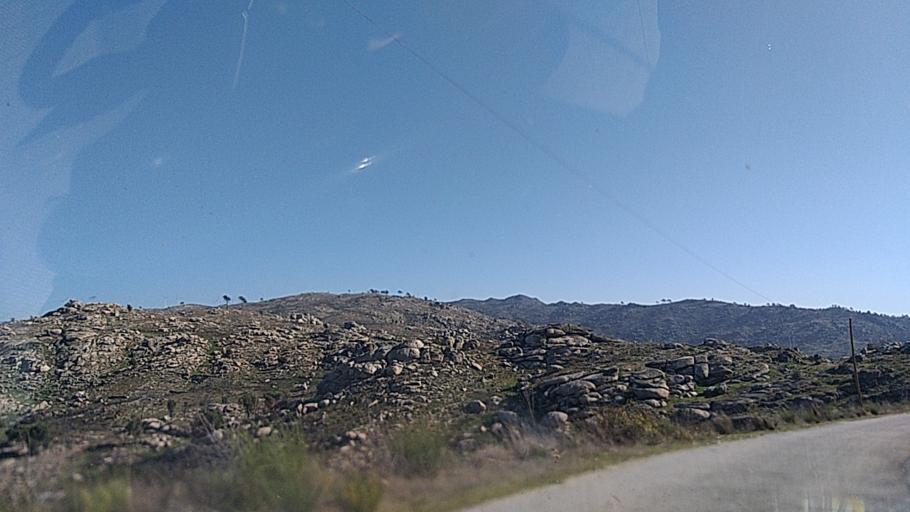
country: PT
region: Guarda
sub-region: Celorico da Beira
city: Celorico da Beira
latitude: 40.6908
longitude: -7.4361
